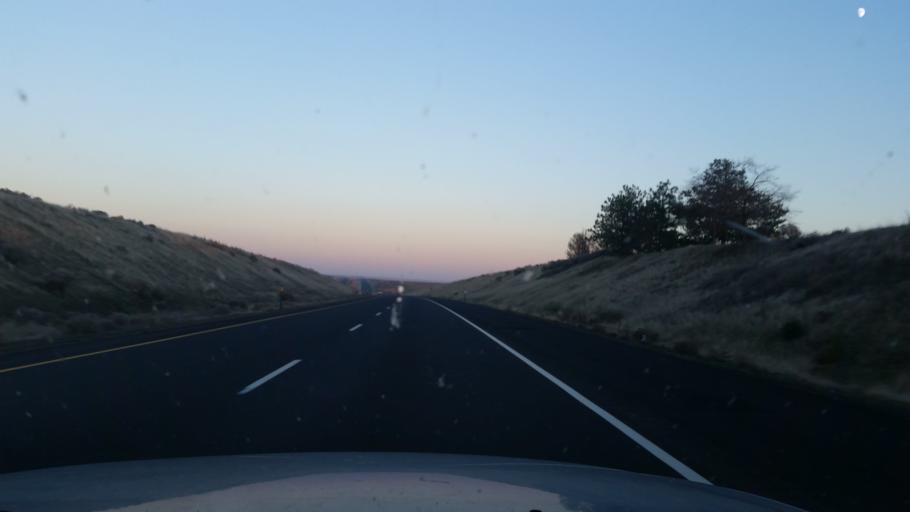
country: US
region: Washington
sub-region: Grant County
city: Warden
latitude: 47.0859
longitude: -118.8456
